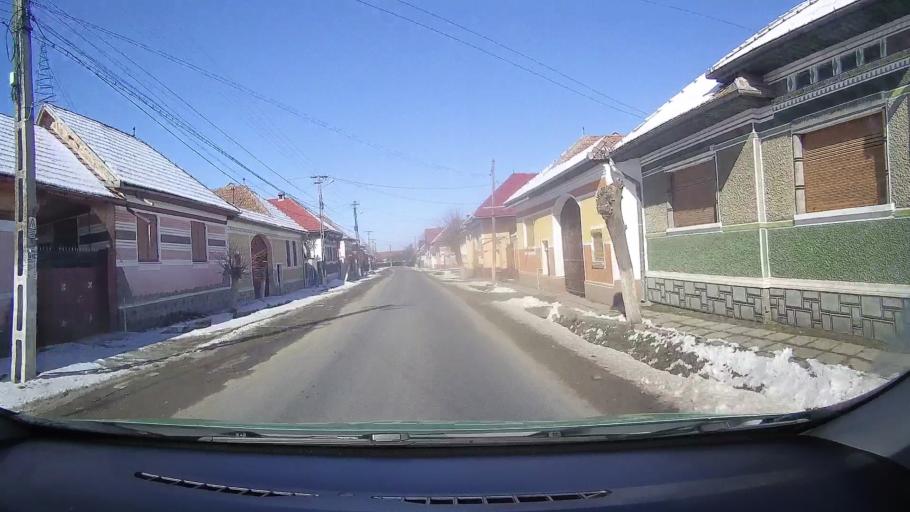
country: RO
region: Brasov
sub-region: Comuna Harseni
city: Harseni
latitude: 45.7567
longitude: 25.0108
